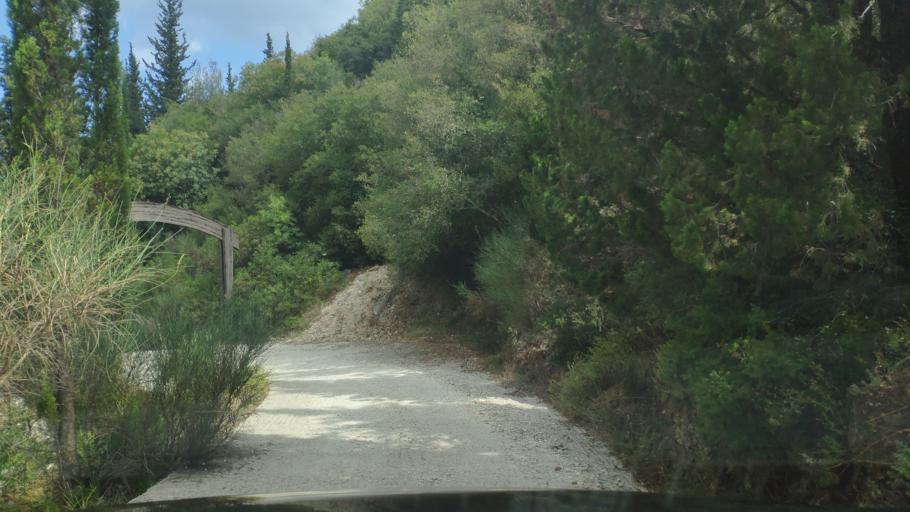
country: GR
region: Ionian Islands
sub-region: Lefkada
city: Lefkada
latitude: 38.7959
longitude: 20.6746
